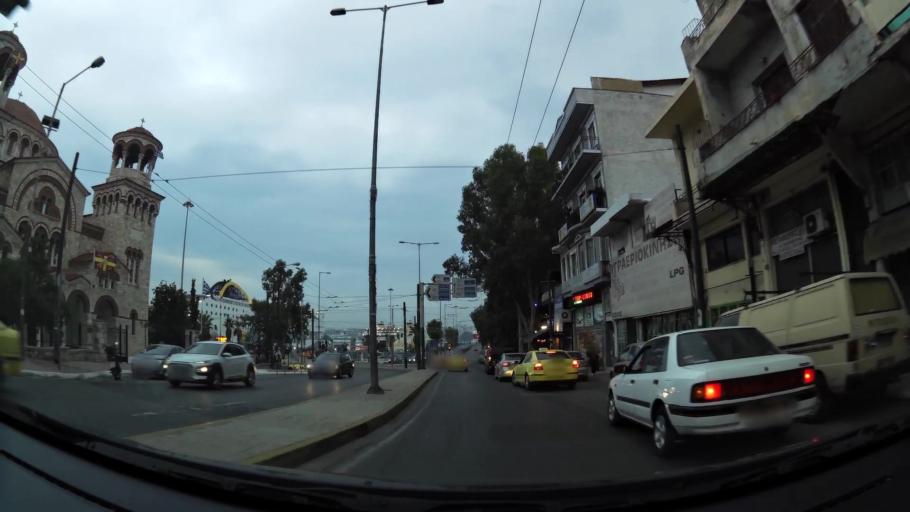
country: GR
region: Attica
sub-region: Nomos Attikis
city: Piraeus
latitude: 37.9499
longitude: 23.6357
